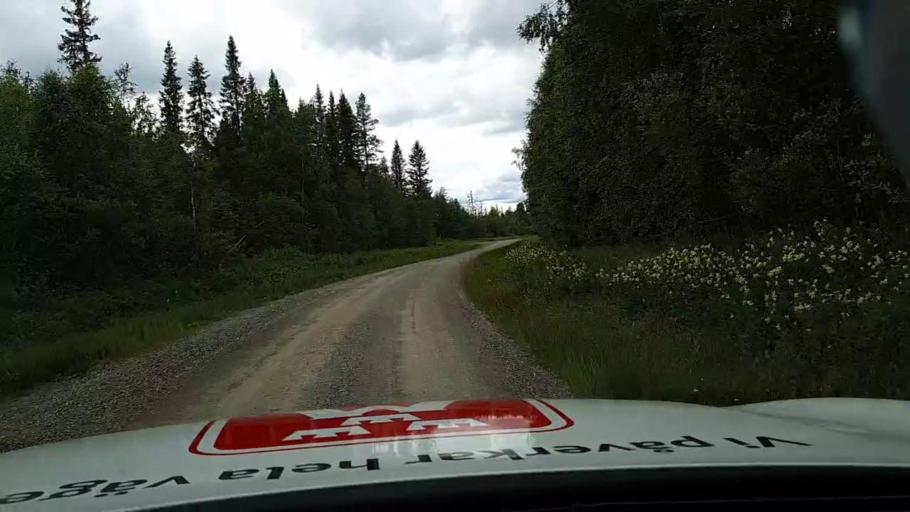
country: SE
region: Jaemtland
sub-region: Stroemsunds Kommun
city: Stroemsund
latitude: 63.3155
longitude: 15.4916
